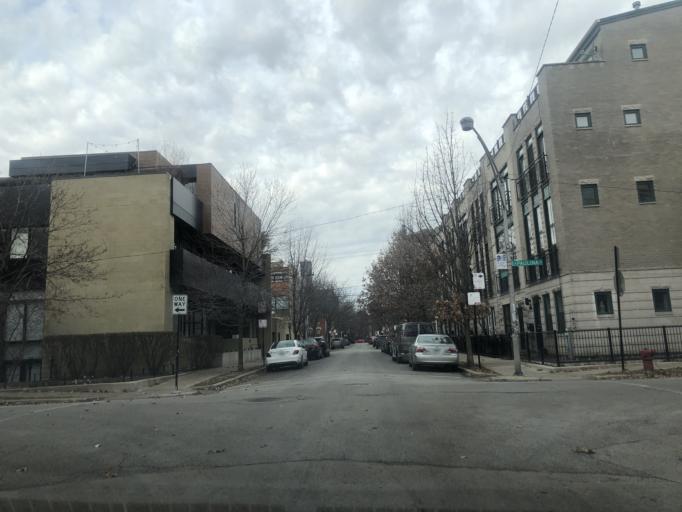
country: US
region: Illinois
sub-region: Cook County
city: Chicago
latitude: 41.8974
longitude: -87.6696
